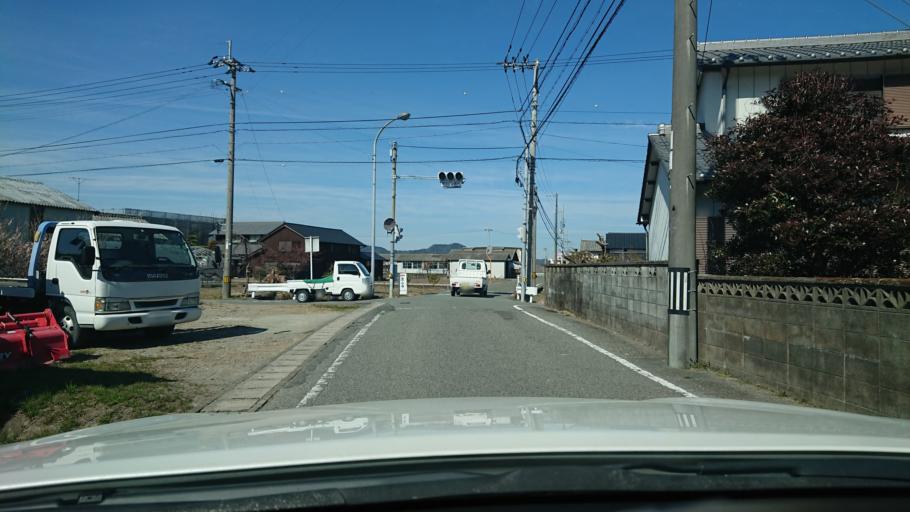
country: JP
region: Tokushima
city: Komatsushimacho
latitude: 33.9833
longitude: 134.5882
